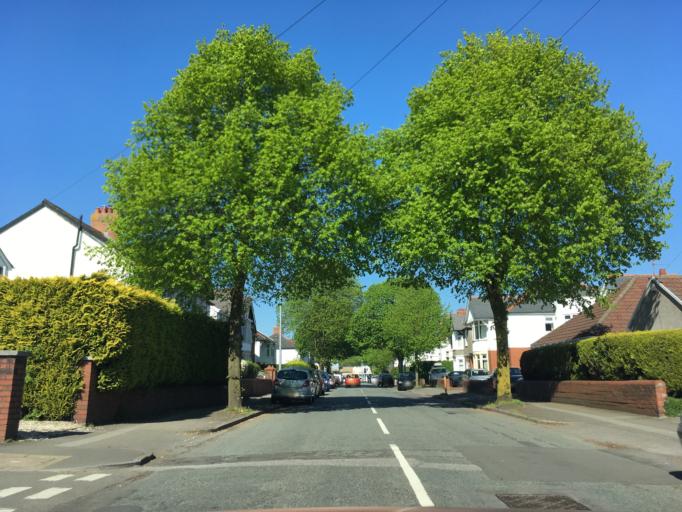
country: GB
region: Wales
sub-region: Cardiff
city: Radyr
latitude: 51.5146
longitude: -3.2266
